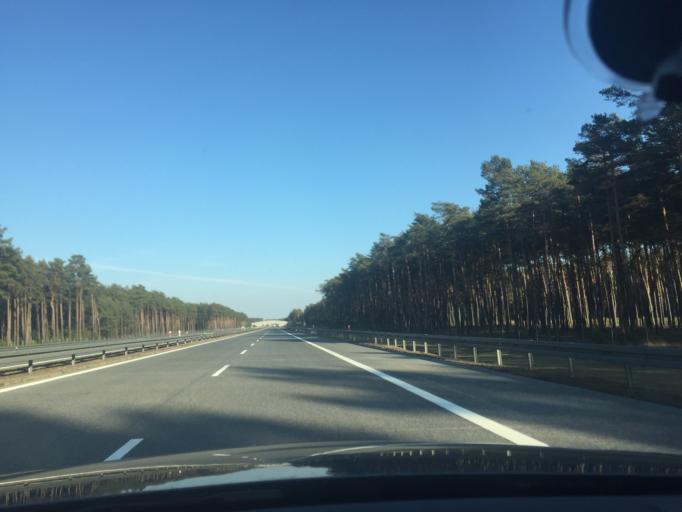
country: PL
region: Greater Poland Voivodeship
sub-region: Powiat nowotomyski
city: Miedzichowo
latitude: 52.3477
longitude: 16.0296
